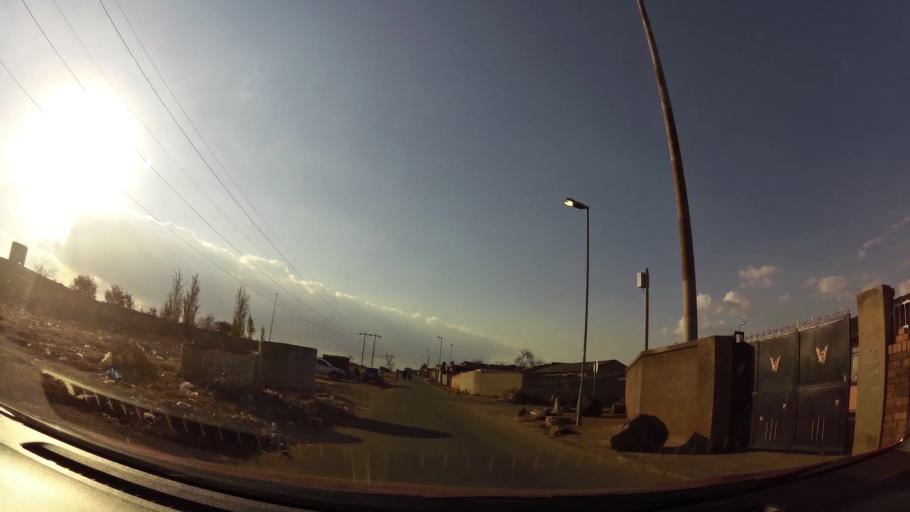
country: ZA
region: Gauteng
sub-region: City of Johannesburg Metropolitan Municipality
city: Soweto
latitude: -26.2337
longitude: 27.8589
